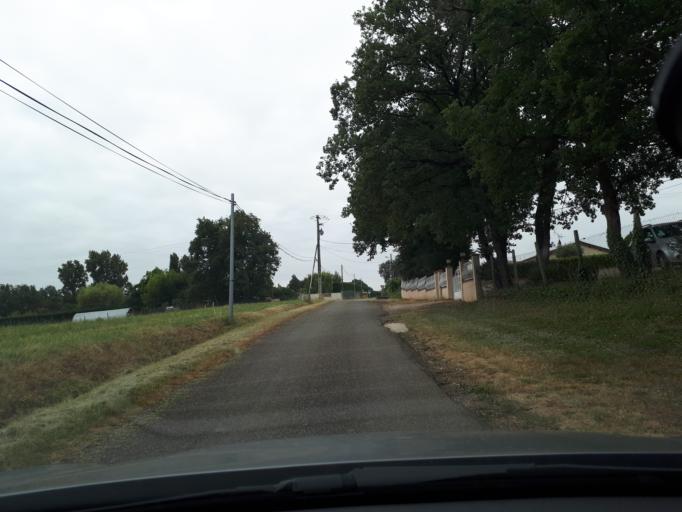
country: FR
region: Midi-Pyrenees
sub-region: Departement du Tarn-et-Garonne
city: Campsas
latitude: 43.8620
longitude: 1.3430
